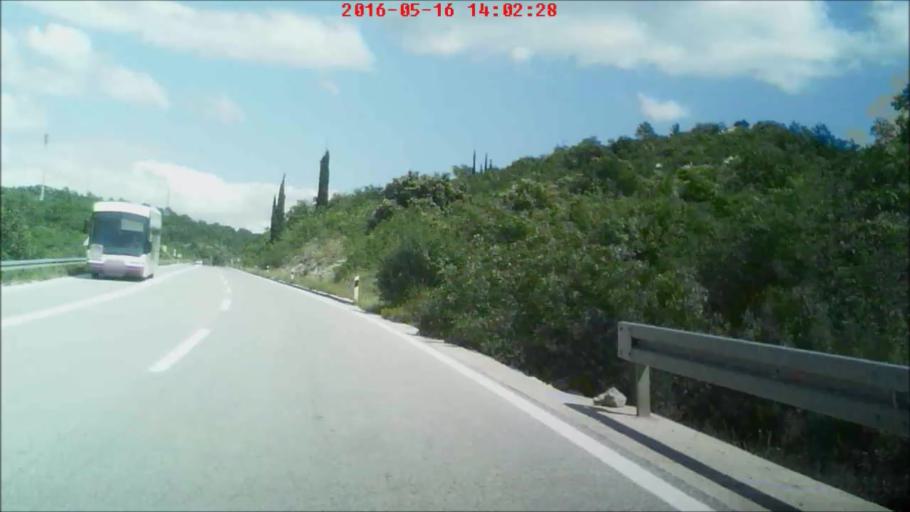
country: HR
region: Dubrovacko-Neretvanska
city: Ston
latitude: 42.8245
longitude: 17.7584
